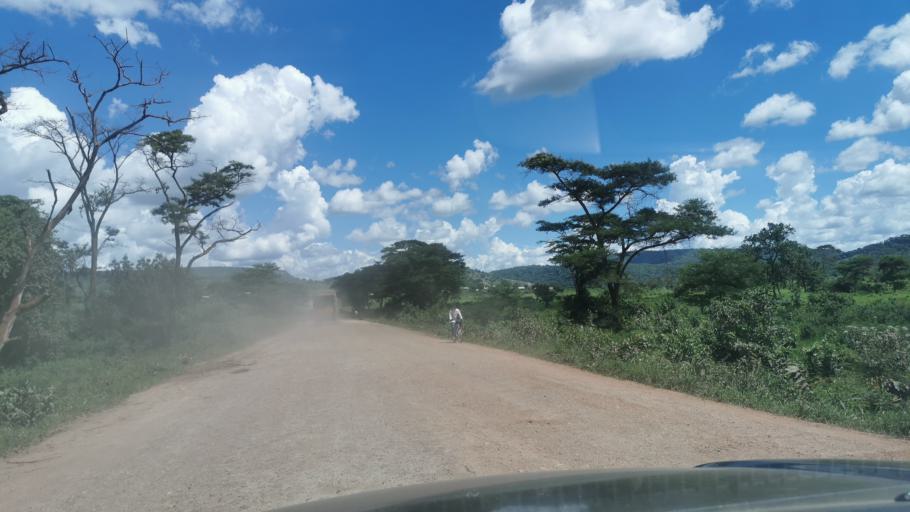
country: TZ
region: Kagera
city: Biharamulo
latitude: -2.8903
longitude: 31.1426
